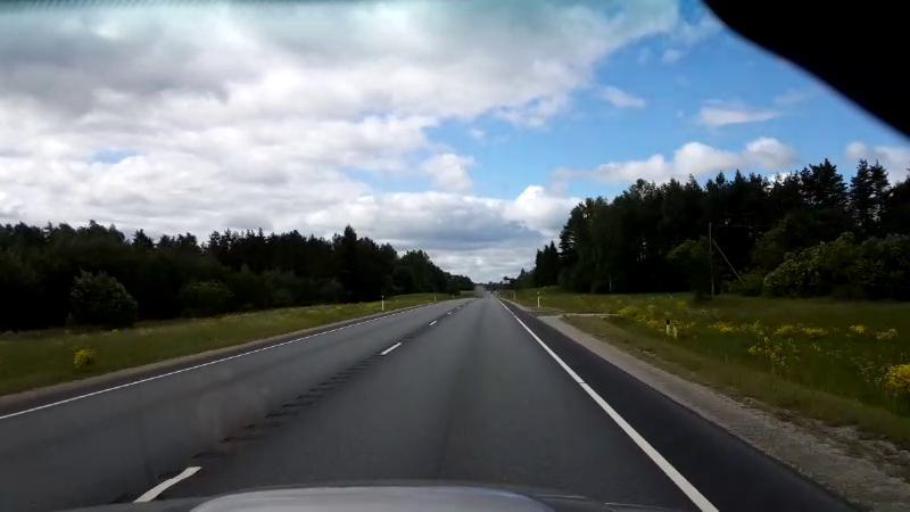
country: EE
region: Harju
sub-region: Nissi vald
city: Riisipere
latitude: 59.0882
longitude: 24.4617
